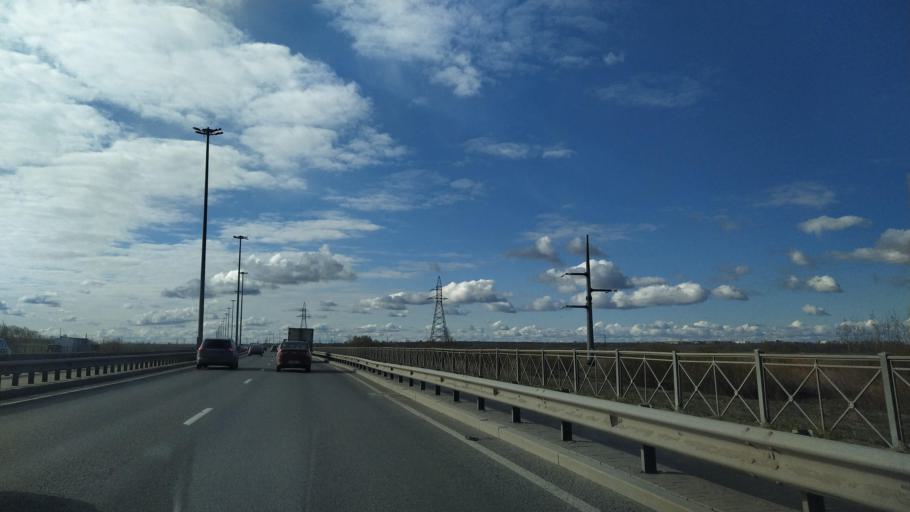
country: RU
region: St.-Petersburg
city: Shushary
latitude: 59.7860
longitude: 30.4014
